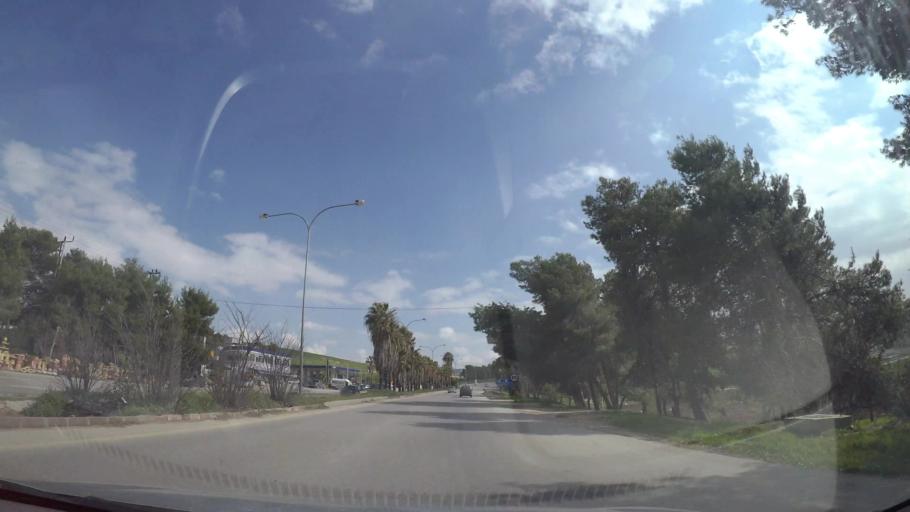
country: JO
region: Balqa
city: As Salt
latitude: 32.0394
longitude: 35.7878
